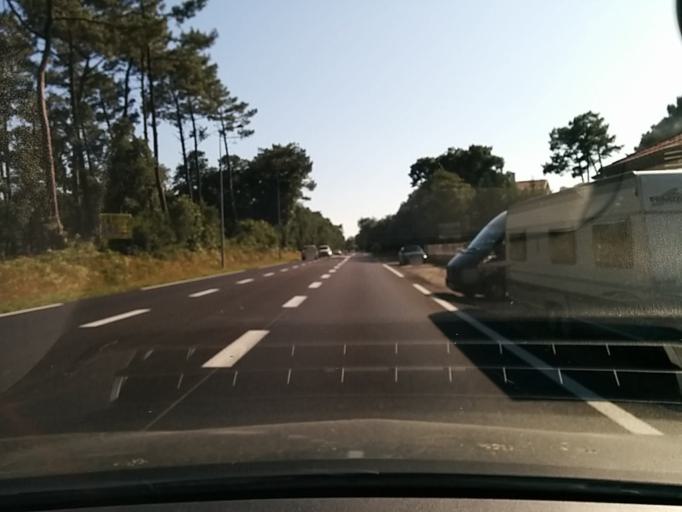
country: FR
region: Aquitaine
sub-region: Departement des Landes
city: Labenne
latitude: 43.6009
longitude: -1.4185
